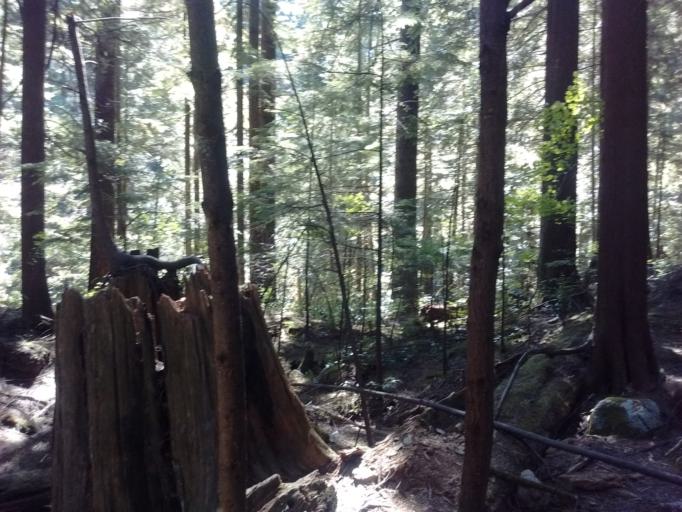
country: CA
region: British Columbia
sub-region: Fraser Valley Regional District
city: North Vancouver
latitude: 49.3437
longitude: -123.0168
